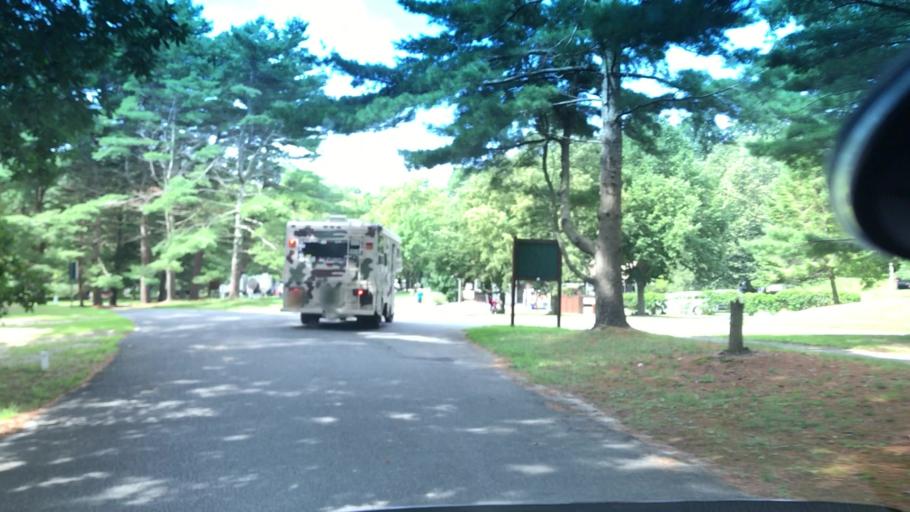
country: US
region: New York
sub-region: Suffolk County
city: Wading River
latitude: 40.9619
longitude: -72.8036
